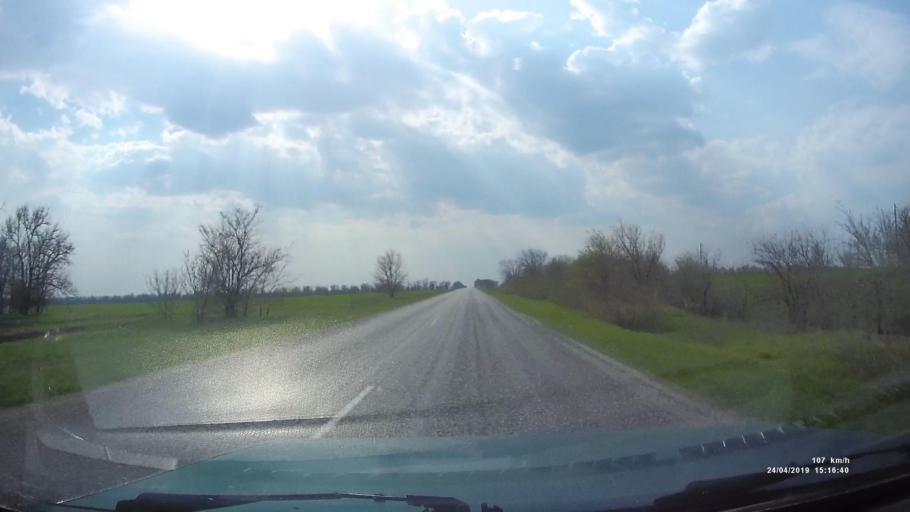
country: RU
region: Rostov
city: Remontnoye
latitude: 46.5463
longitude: 43.2064
